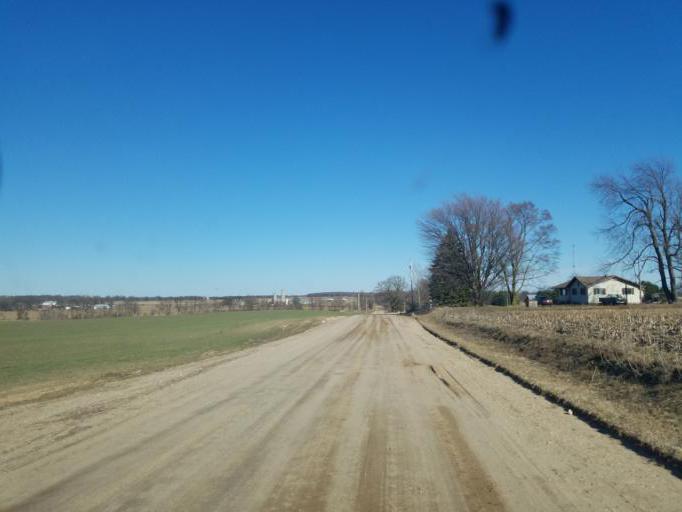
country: US
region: Michigan
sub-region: Montcalm County
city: Edmore
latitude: 43.4949
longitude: -85.0760
